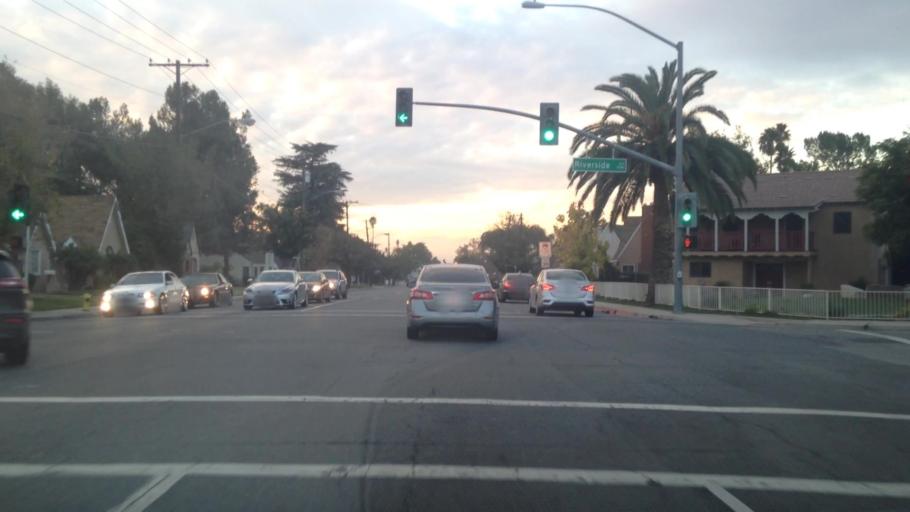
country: US
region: California
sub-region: Riverside County
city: Riverside
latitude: 33.9610
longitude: -117.3877
